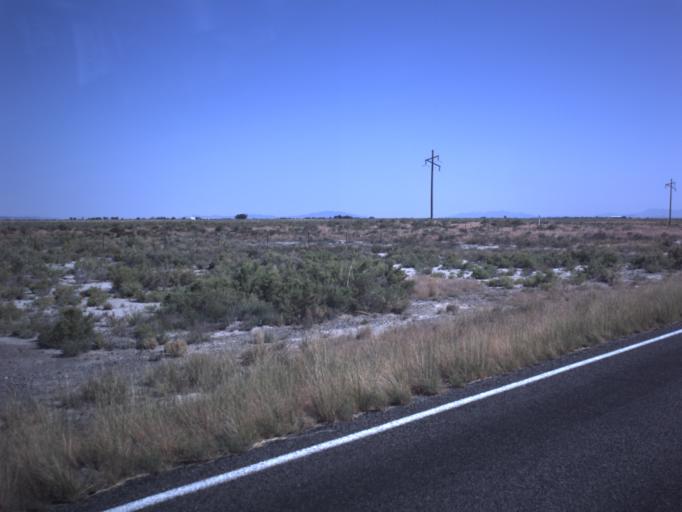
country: US
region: Utah
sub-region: Millard County
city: Delta
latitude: 39.2130
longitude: -112.6800
